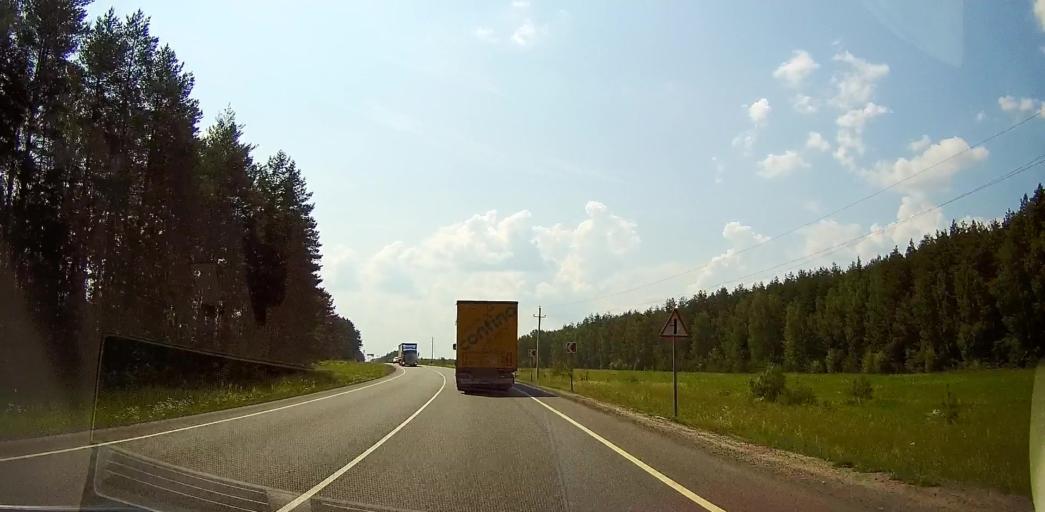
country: RU
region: Moskovskaya
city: Meshcherino
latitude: 55.1779
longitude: 38.3387
